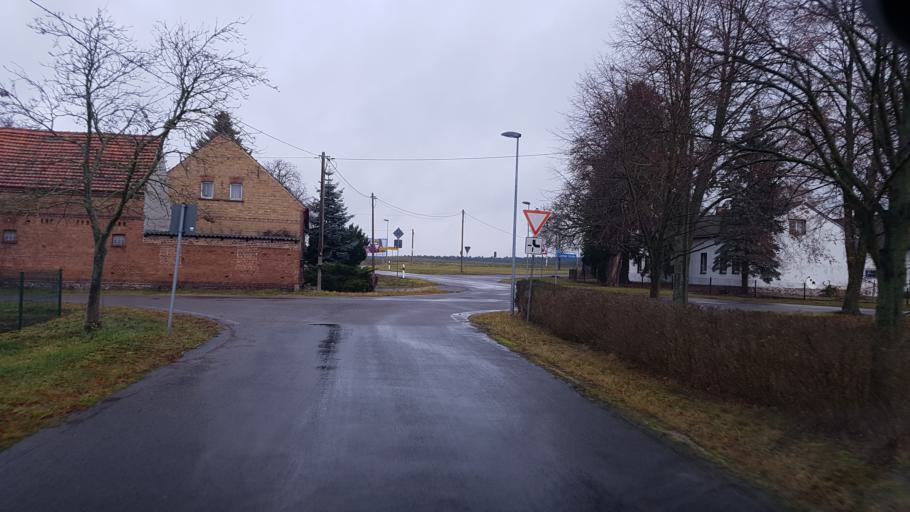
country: DE
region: Brandenburg
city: Bronkow
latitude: 51.6515
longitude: 13.8957
